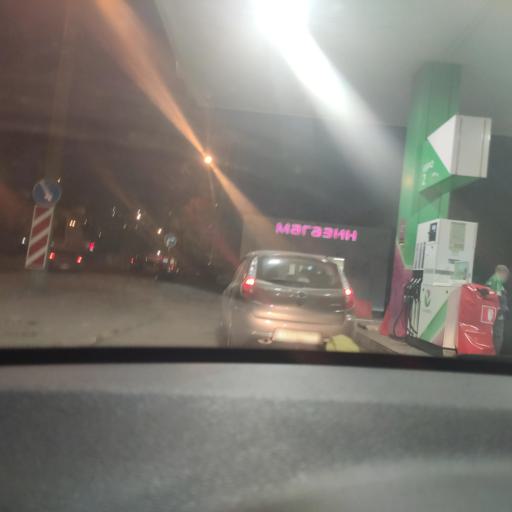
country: RU
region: Samara
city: Samara
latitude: 53.1936
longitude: 50.1640
